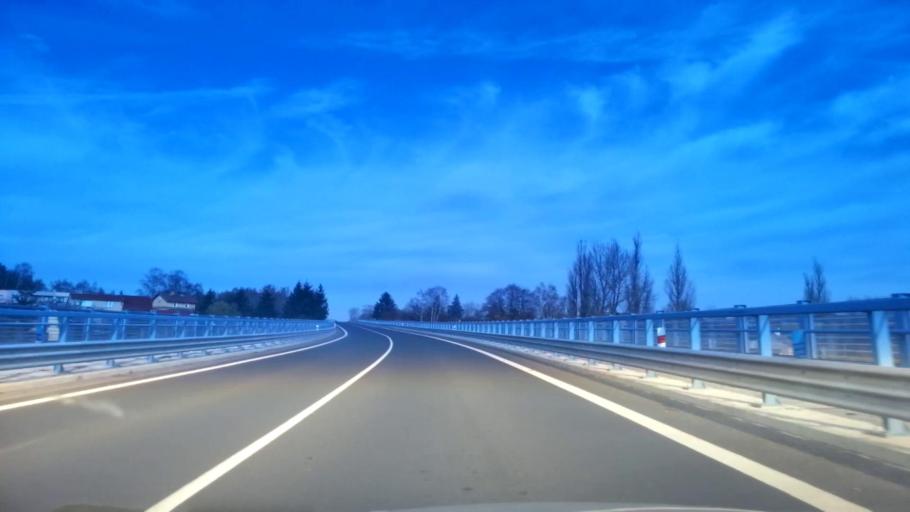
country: CZ
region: Karlovarsky
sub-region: Okres Cheb
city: Cheb
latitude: 50.0590
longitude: 12.3813
